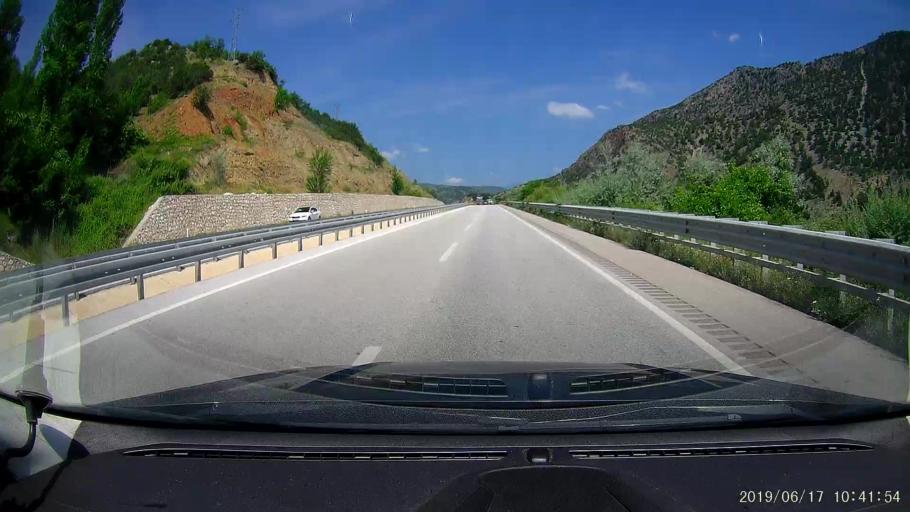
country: TR
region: Corum
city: Kargi
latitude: 41.0443
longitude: 34.5656
